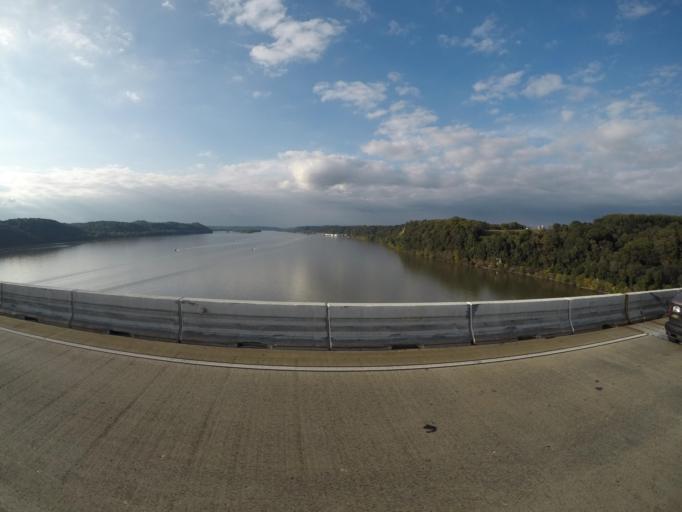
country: US
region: Maryland
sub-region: Harford County
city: Havre de Grace
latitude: 39.5821
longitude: -76.1014
